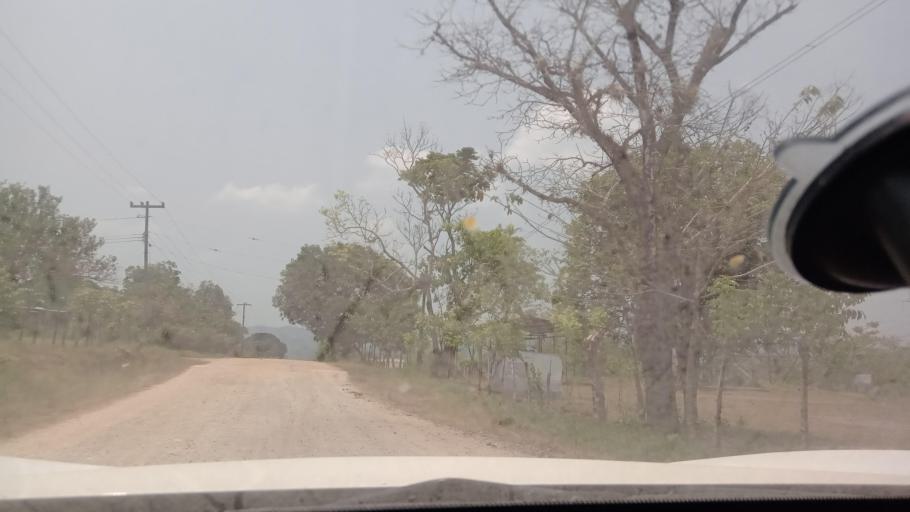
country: MX
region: Chiapas
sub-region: Tecpatan
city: Raudales Malpaso
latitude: 17.4509
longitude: -93.7922
